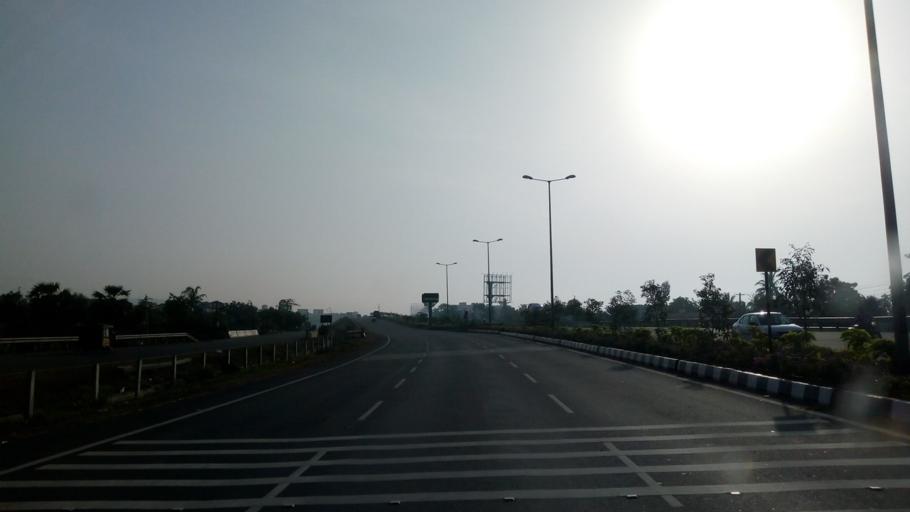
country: IN
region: Andhra Pradesh
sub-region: Guntur
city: Mangalagiri
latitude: 16.3924
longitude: 80.5415
